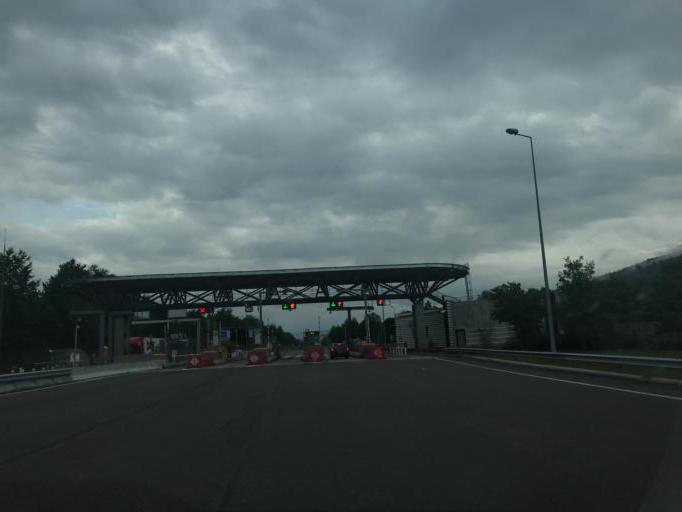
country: FR
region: Rhone-Alpes
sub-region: Departement de l'Ain
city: Groissiat
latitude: 46.2231
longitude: 5.6136
